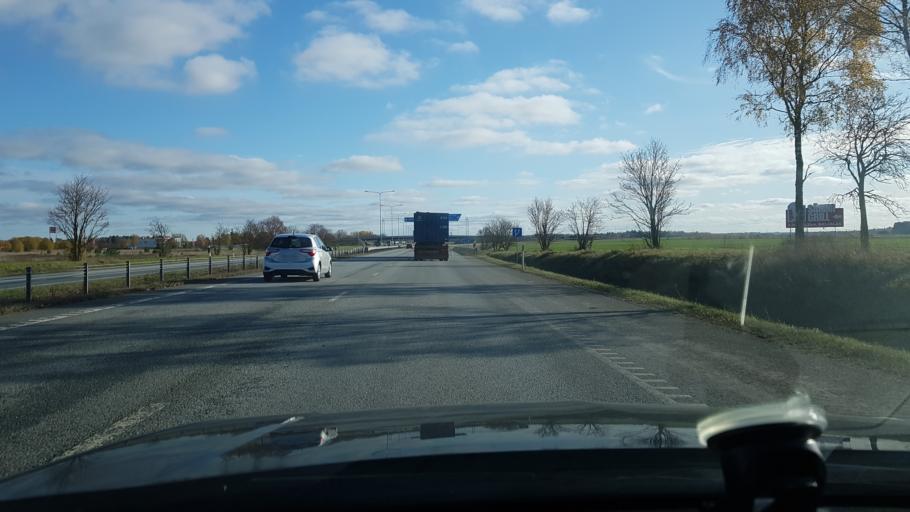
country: EE
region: Laeaene-Virumaa
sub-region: Haljala vald
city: Haljala
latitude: 59.4251
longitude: 26.2590
